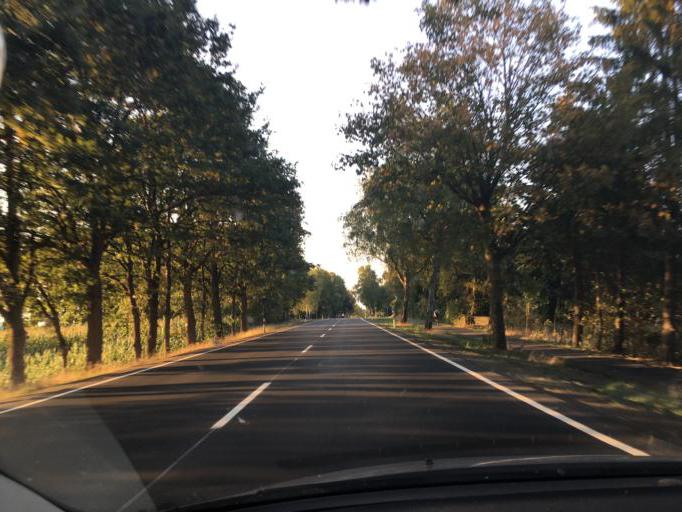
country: DE
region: Lower Saxony
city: Bergen
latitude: 52.7883
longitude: 9.9730
